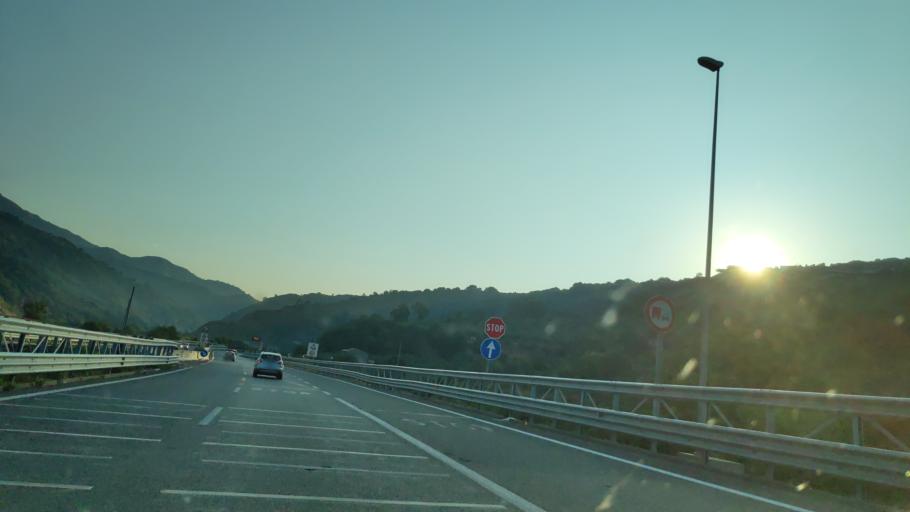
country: IT
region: Calabria
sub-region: Provincia di Catanzaro
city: San Mango d'Aquino
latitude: 39.0653
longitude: 16.1796
